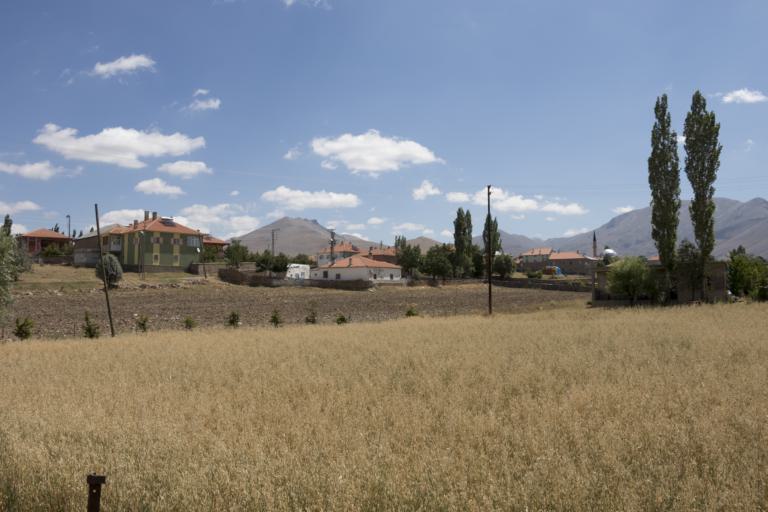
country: TR
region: Kayseri
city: Toklar
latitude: 38.4064
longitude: 36.0768
